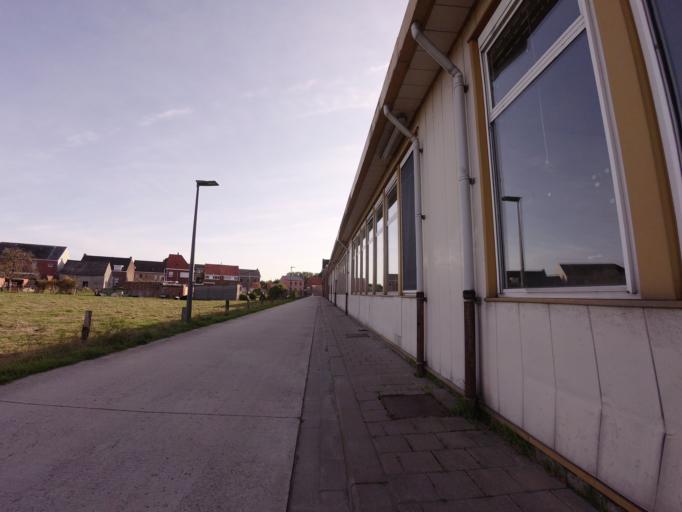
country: BE
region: Flanders
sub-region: Provincie Antwerpen
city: Stabroek
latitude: 51.3456
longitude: 4.3164
